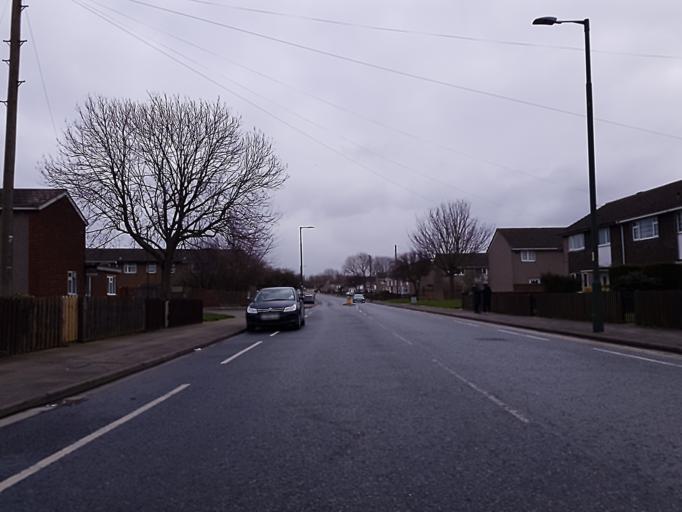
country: GB
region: England
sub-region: North East Lincolnshire
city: Great Coates
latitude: 53.5714
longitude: -0.1248
